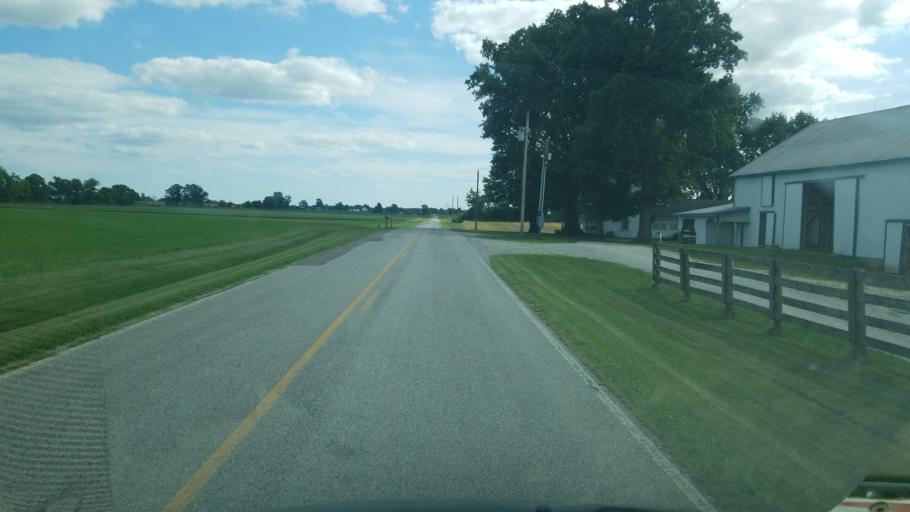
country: US
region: Ohio
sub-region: Champaign County
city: Saint Paris
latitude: 40.2053
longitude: -83.9425
